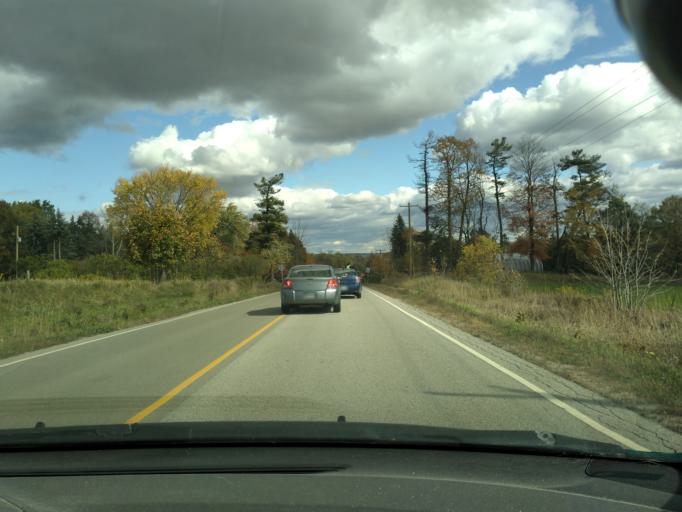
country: CA
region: Ontario
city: Bradford West Gwillimbury
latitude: 44.0847
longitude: -79.5819
